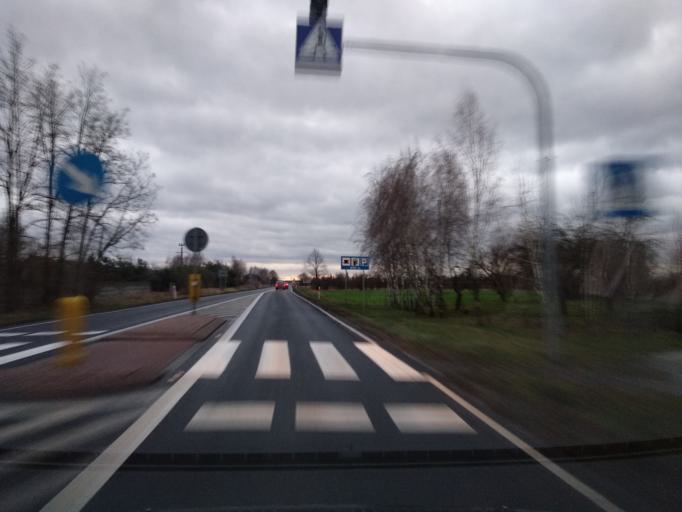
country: PL
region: Greater Poland Voivodeship
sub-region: Powiat koninski
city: Rychwal
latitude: 52.0777
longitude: 18.1599
